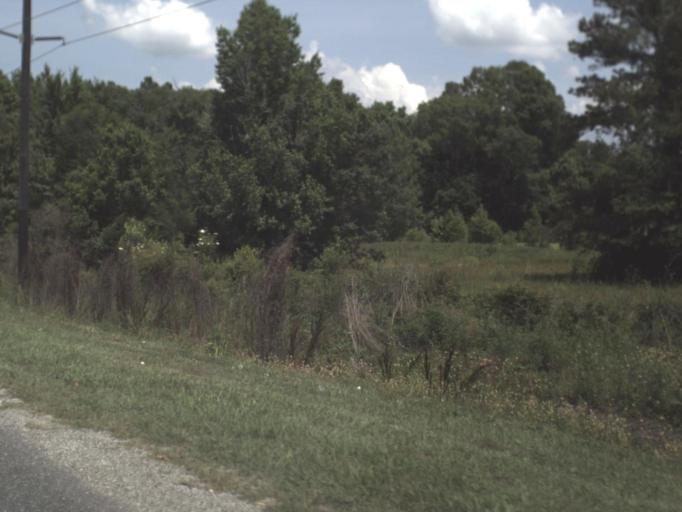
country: US
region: Florida
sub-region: Union County
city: Lake Butler
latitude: 29.9975
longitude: -82.2725
